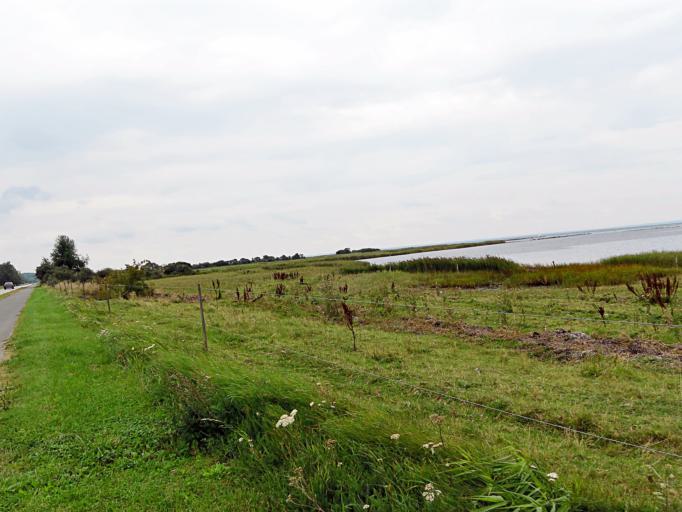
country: DK
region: Capital Region
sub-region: Fredensborg Kommune
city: Niva
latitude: 55.9267
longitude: 12.5184
